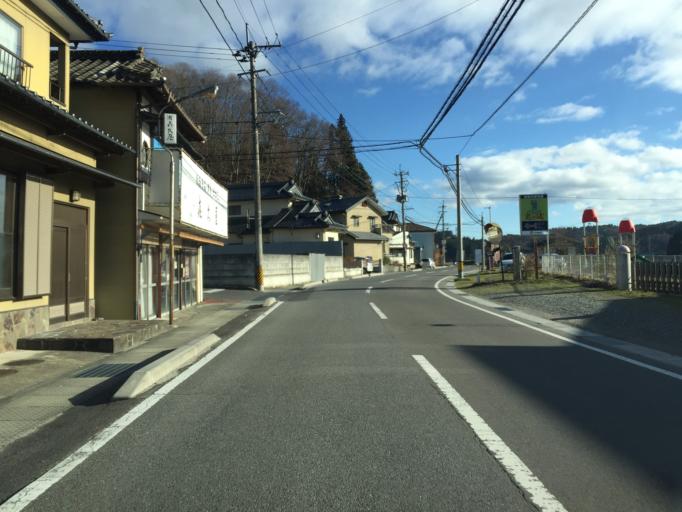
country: JP
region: Fukushima
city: Funehikimachi-funehiki
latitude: 37.2534
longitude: 140.6630
